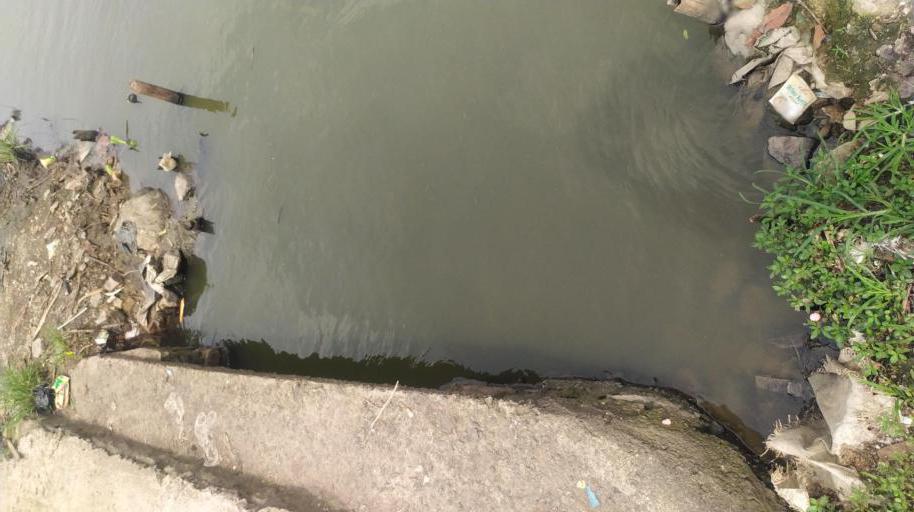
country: ID
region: West Java
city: Ciputat
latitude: -6.1996
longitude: 106.6754
